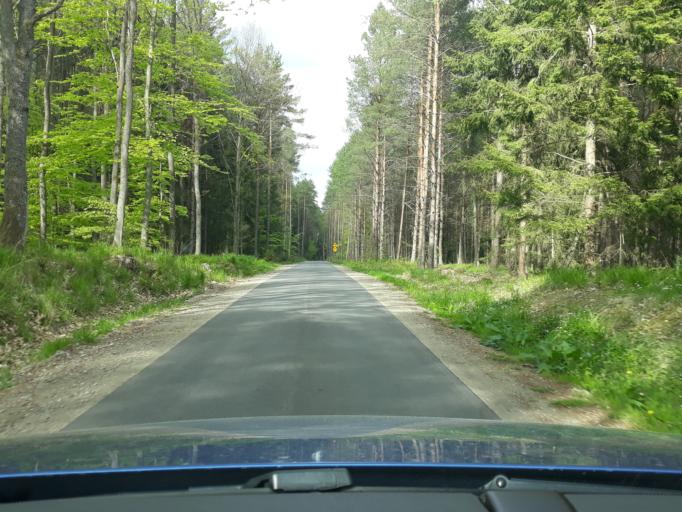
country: PL
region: Pomeranian Voivodeship
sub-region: Powiat czluchowski
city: Czluchow
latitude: 53.7398
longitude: 17.3465
